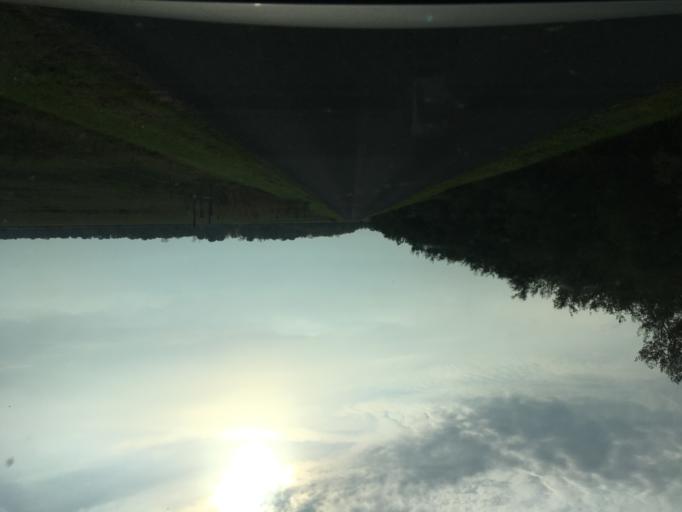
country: AT
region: Burgenland
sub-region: Politischer Bezirk Neusiedl am See
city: Apetlon
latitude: 47.6921
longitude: 16.8388
